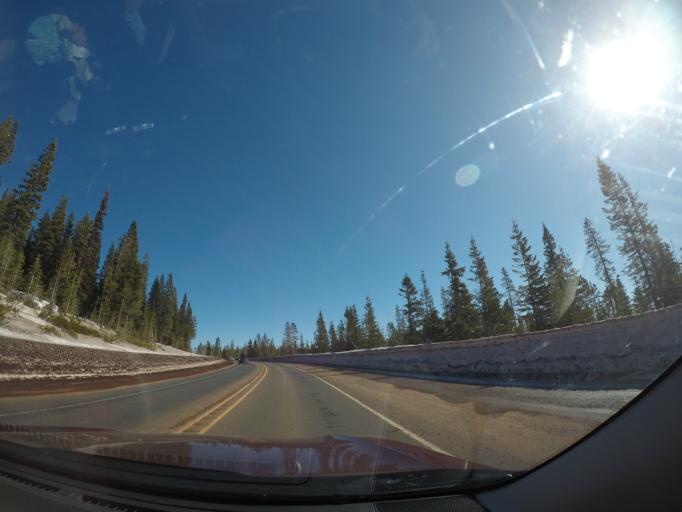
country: US
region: Oregon
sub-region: Deschutes County
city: Sunriver
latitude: 43.9802
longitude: -121.5857
